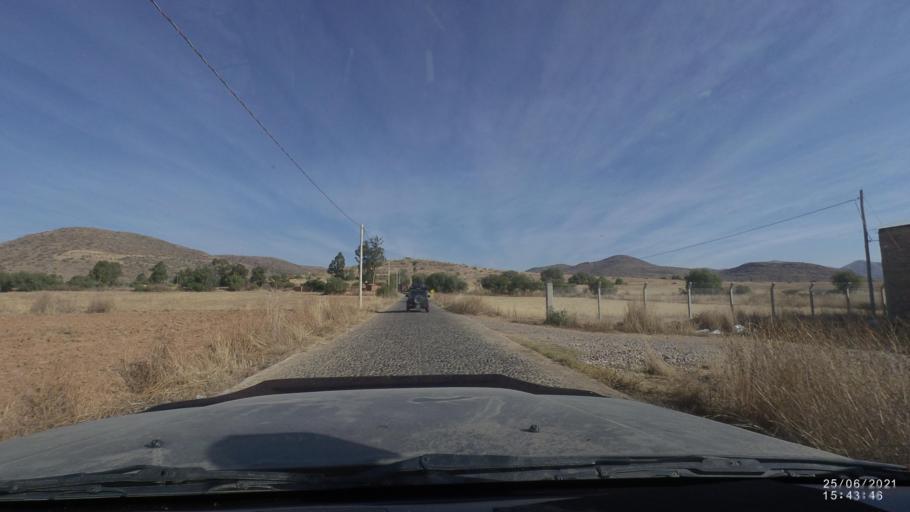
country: BO
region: Cochabamba
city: Cliza
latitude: -17.6519
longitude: -65.9129
